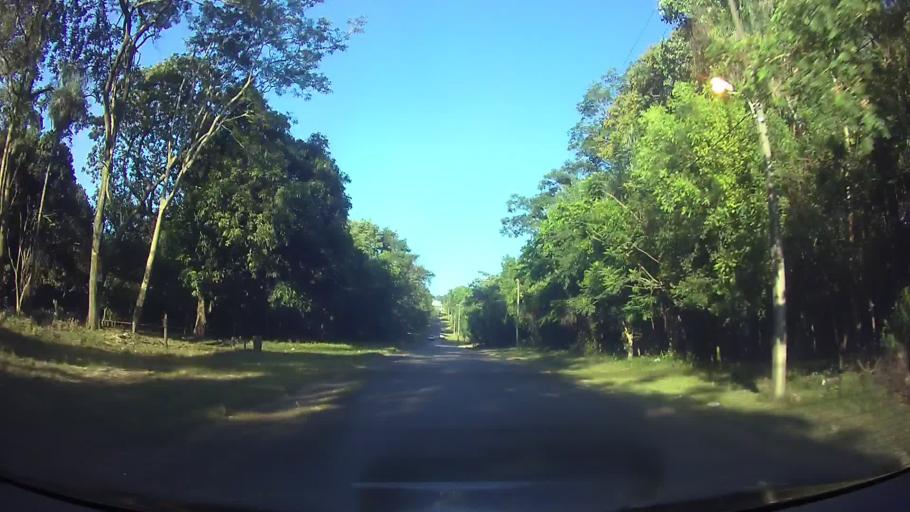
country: PY
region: Cordillera
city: San Bernardino
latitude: -25.3187
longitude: -57.2704
